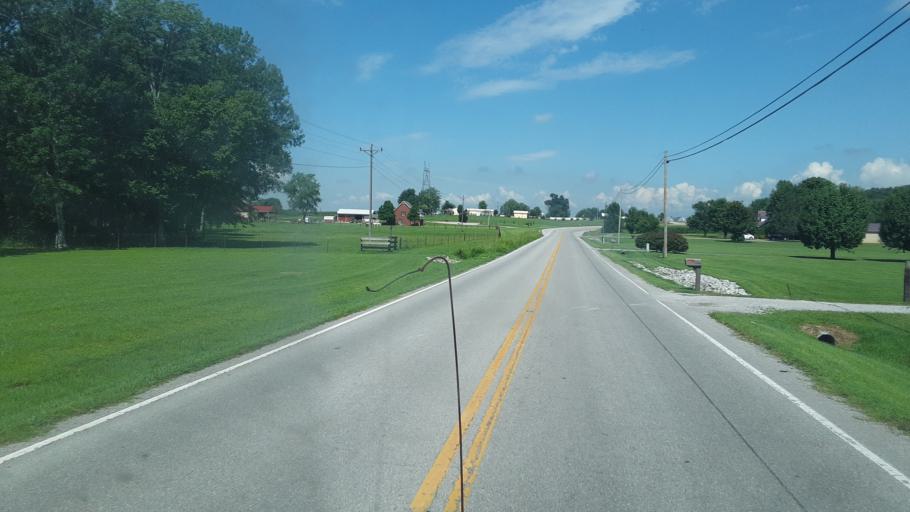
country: US
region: Kentucky
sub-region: Todd County
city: Elkton
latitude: 36.8197
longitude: -87.1957
